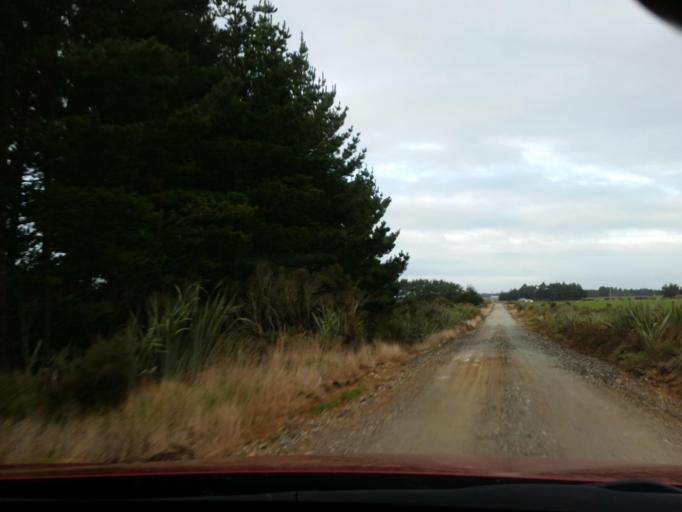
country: NZ
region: Southland
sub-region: Invercargill City
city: Bluff
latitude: -46.5324
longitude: 168.5626
